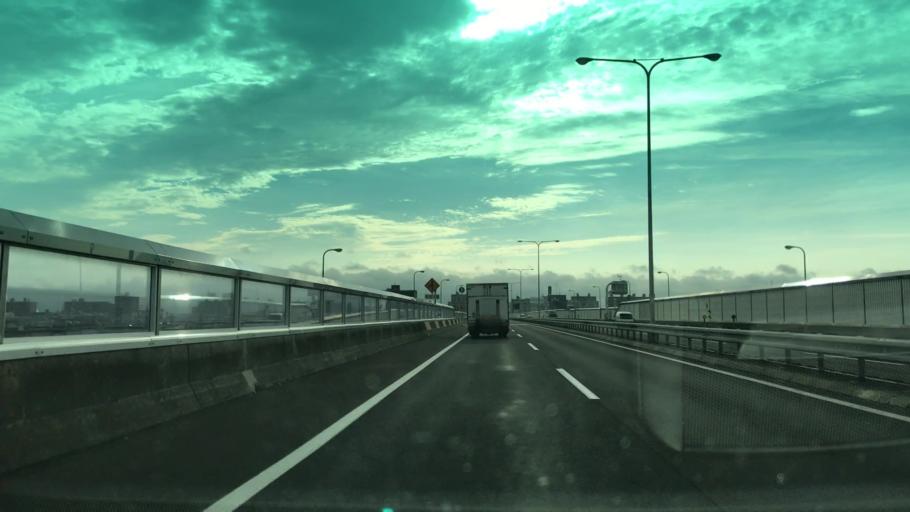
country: JP
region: Hokkaido
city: Sapporo
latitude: 43.1023
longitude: 141.3540
